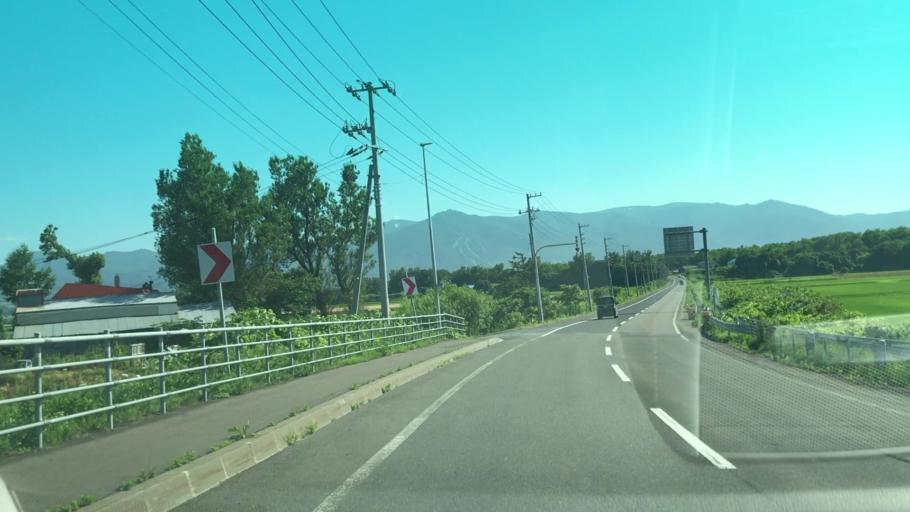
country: JP
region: Hokkaido
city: Iwanai
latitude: 43.0207
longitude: 140.5477
